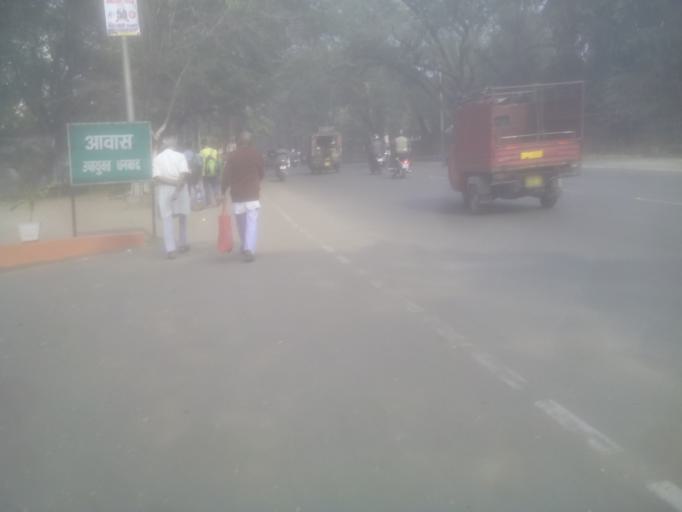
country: IN
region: Jharkhand
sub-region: Dhanbad
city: Dhanbad
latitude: 23.8033
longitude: 86.4276
